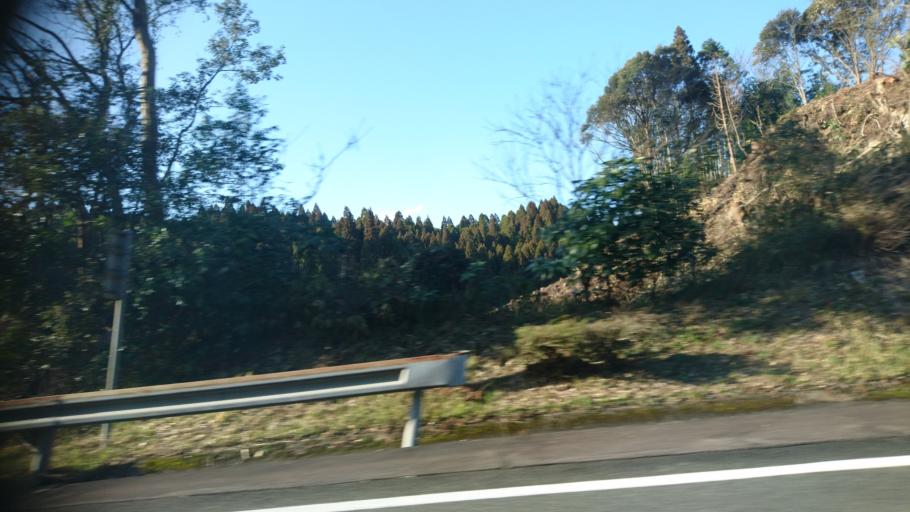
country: JP
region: Miyazaki
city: Kobayashi
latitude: 32.0321
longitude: 130.8062
